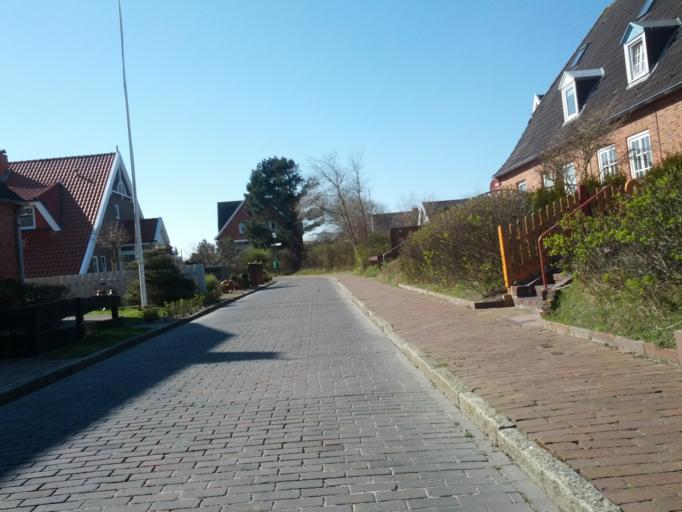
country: DE
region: Lower Saxony
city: Langeoog
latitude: 53.7520
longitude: 7.4863
